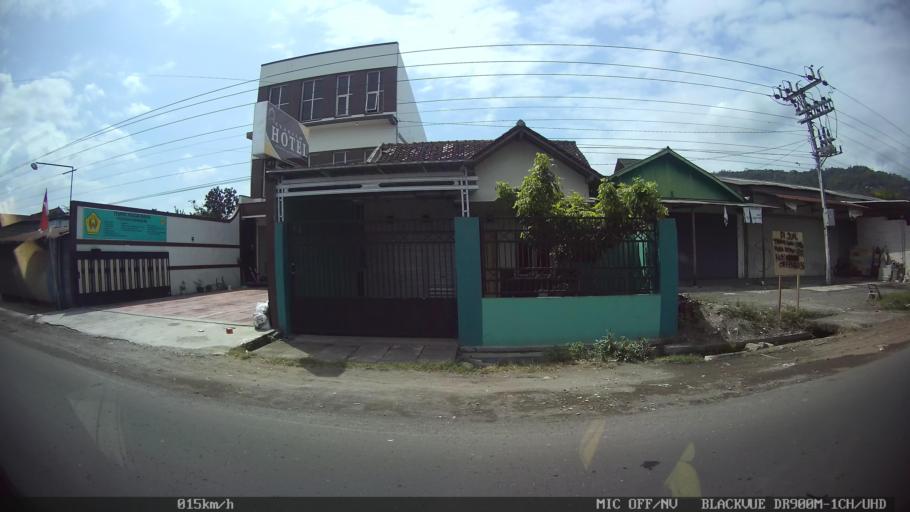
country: ID
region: Daerah Istimewa Yogyakarta
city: Depok
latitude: -7.8350
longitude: 110.4769
